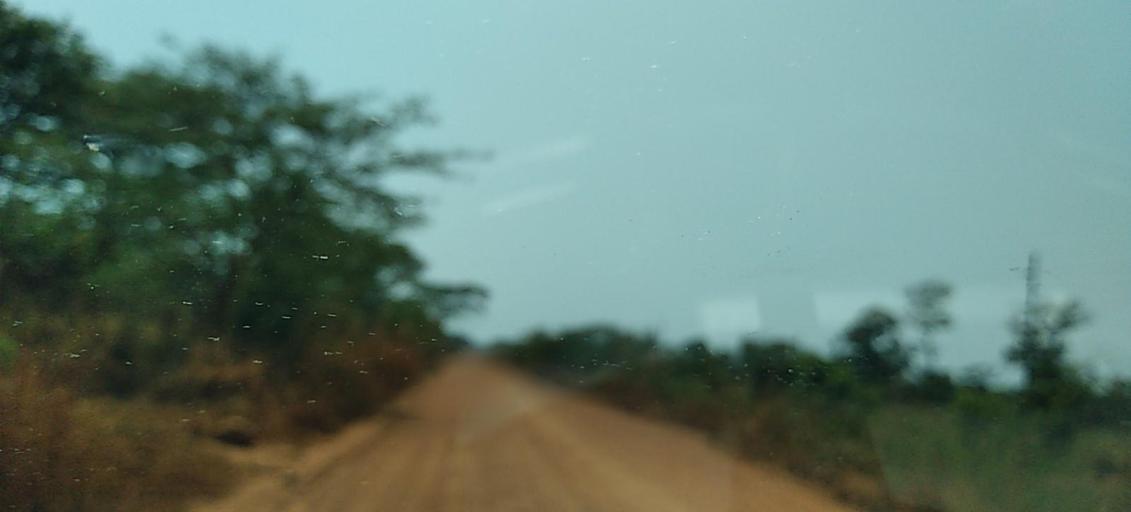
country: ZM
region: North-Western
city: Kansanshi
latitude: -12.0055
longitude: 26.5374
